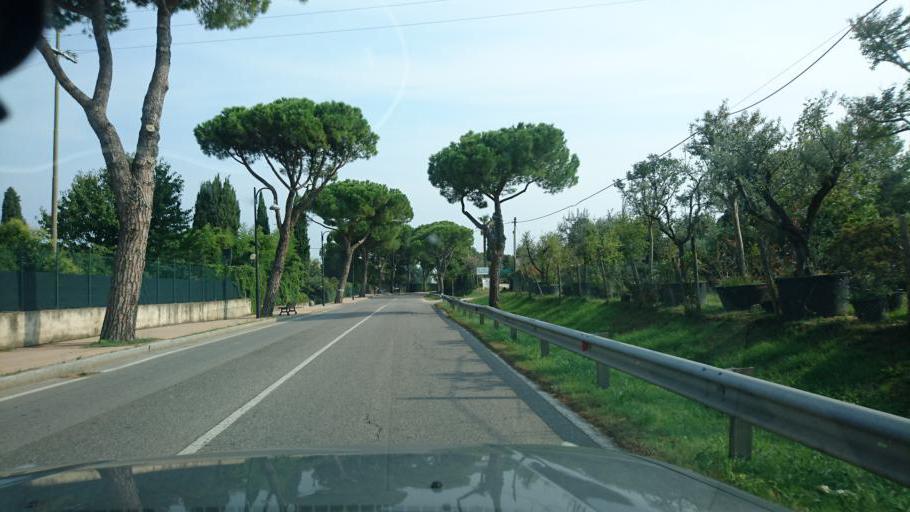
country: IT
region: Lombardy
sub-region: Provincia di Brescia
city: Padenghe sul Garda
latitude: 45.4867
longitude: 10.5367
